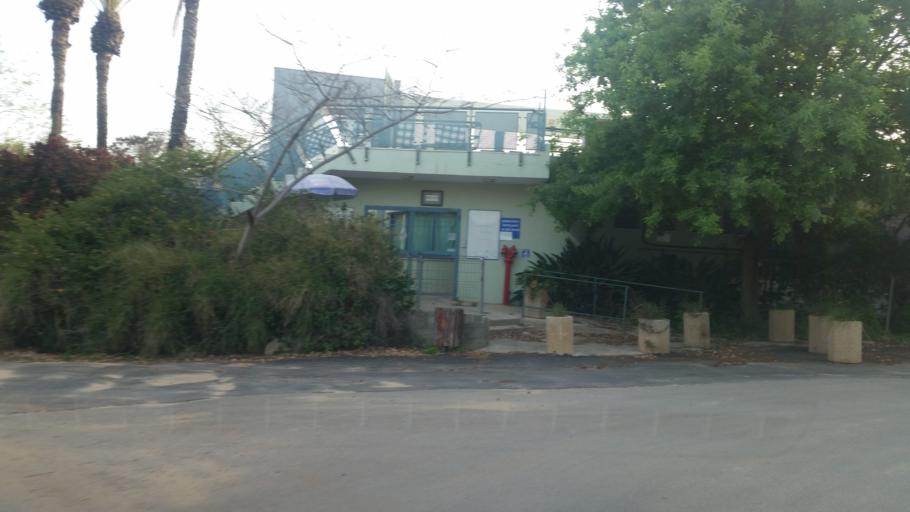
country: IL
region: Tel Aviv
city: Herzliyya
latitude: 32.1572
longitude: 34.8332
